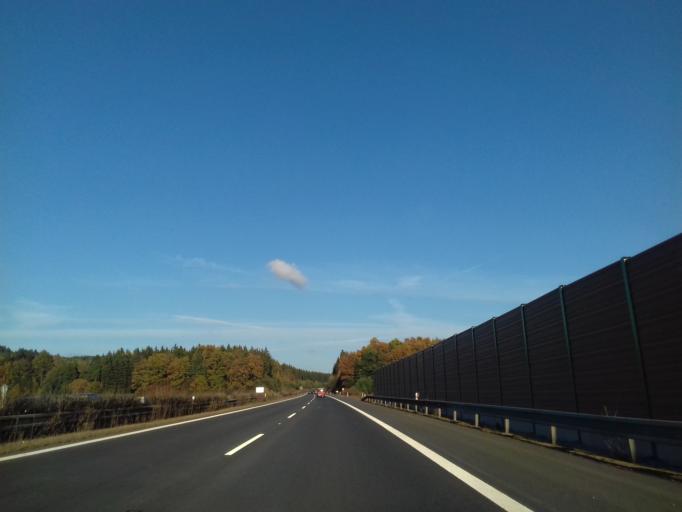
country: CZ
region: Plzensky
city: Holoubkov
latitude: 49.7649
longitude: 13.6447
